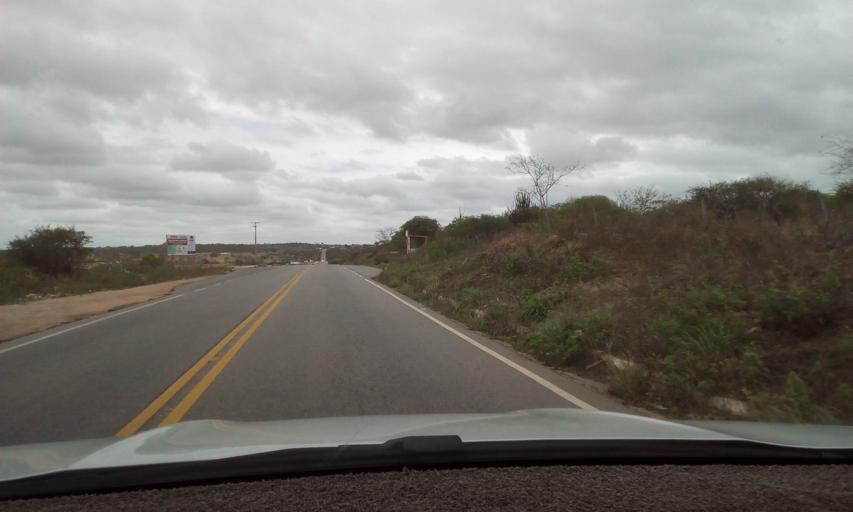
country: BR
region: Paraiba
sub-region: Cuite
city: Cuite
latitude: -6.5972
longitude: -36.2309
